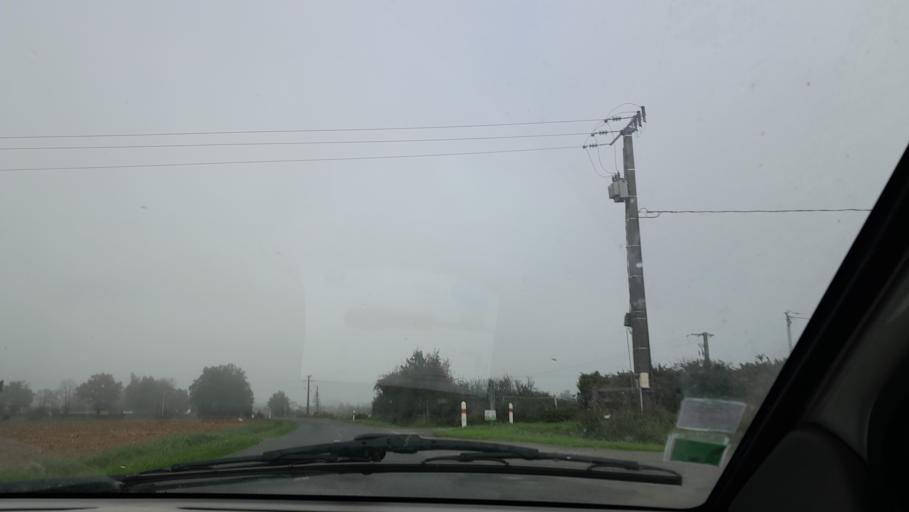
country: FR
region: Pays de la Loire
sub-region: Departement de la Mayenne
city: Saint-Pierre-la-Cour
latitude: 48.1292
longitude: -1.0228
